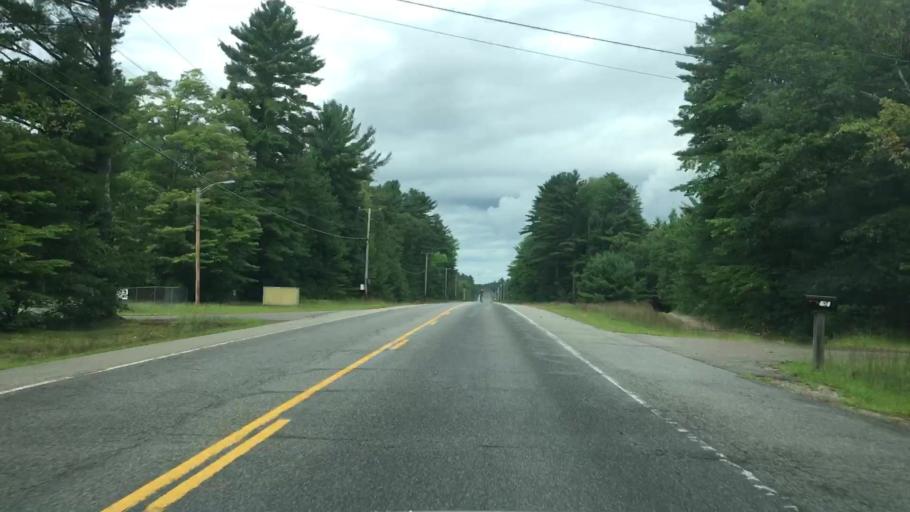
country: US
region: Maine
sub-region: York County
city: South Sanford
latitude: 43.3802
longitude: -70.7405
